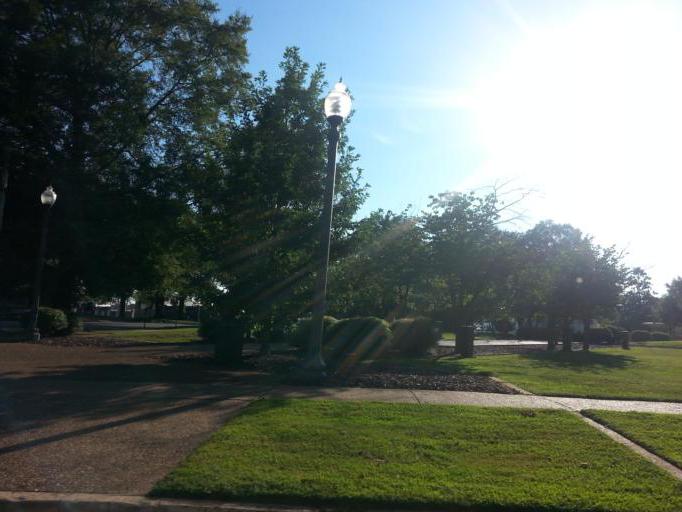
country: US
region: Alabama
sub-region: Lauderdale County
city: Florence
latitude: 34.8033
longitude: -87.6746
